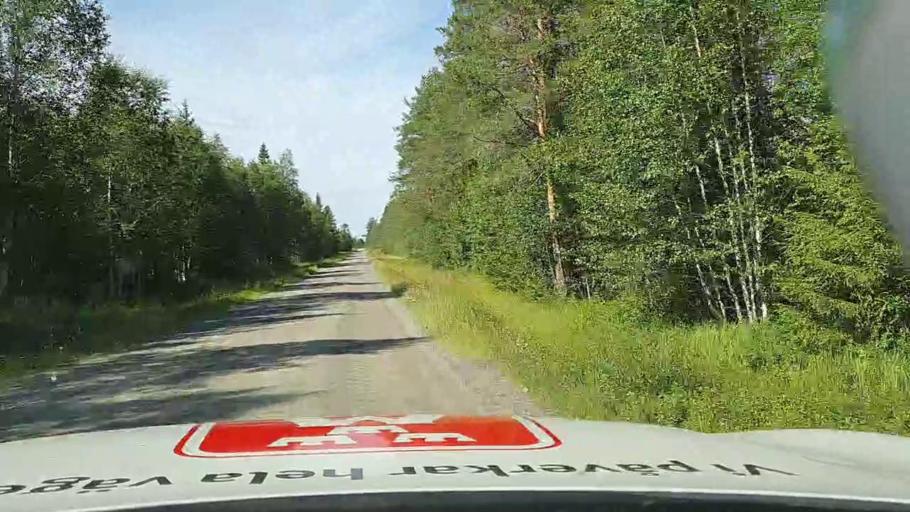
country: SE
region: Jaemtland
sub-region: Stroemsunds Kommun
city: Stroemsund
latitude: 63.7088
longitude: 15.3157
